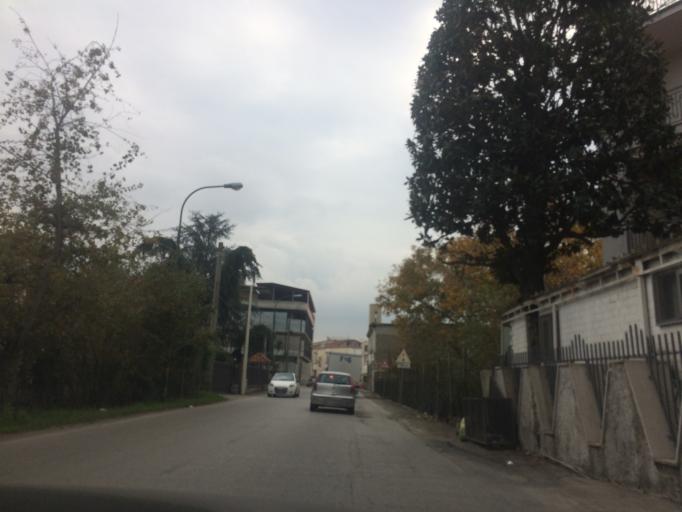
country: IT
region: Campania
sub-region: Provincia di Napoli
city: Piazzolla
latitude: 40.8807
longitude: 14.5290
